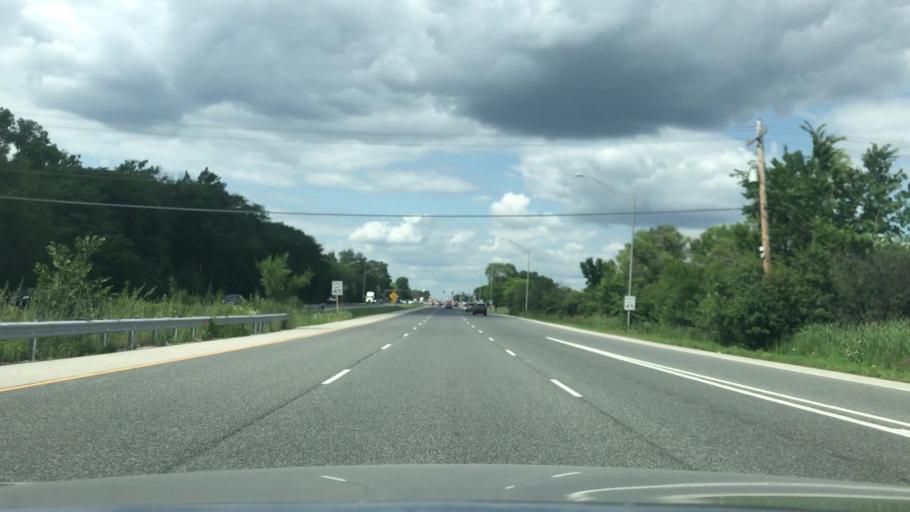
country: US
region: Illinois
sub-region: DuPage County
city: Burr Ridge
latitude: 41.7447
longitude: -87.9443
